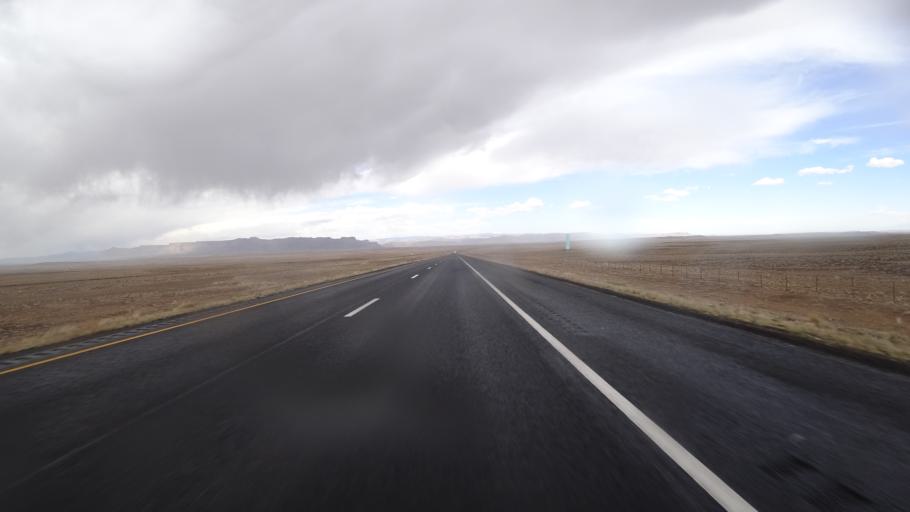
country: US
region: Utah
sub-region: Carbon County
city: East Carbon City
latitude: 38.9420
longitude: -110.3312
